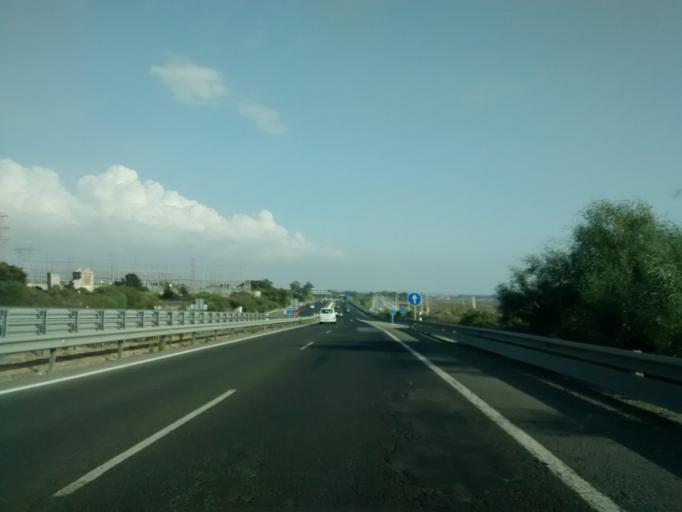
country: ES
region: Andalusia
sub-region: Provincia de Cadiz
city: Puerto Real
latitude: 36.5202
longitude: -6.1606
